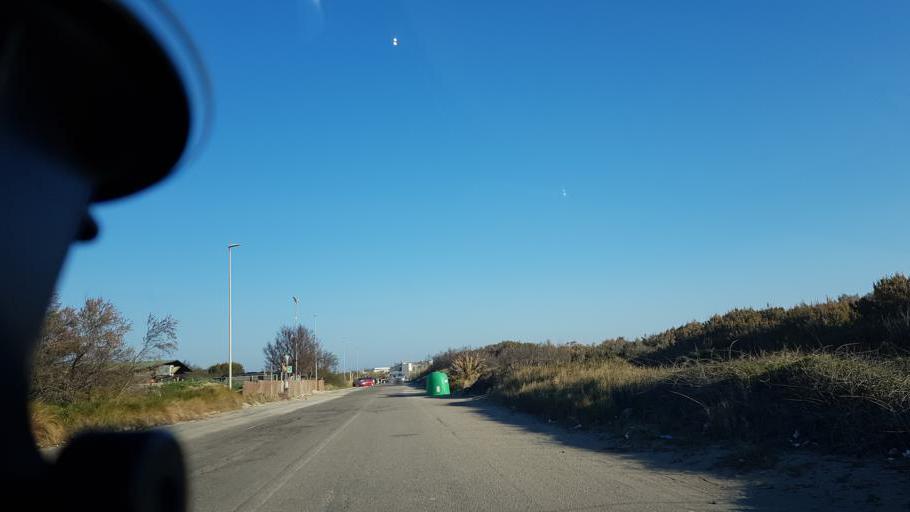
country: IT
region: Apulia
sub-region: Provincia di Lecce
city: Struda
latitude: 40.3937
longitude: 18.3015
